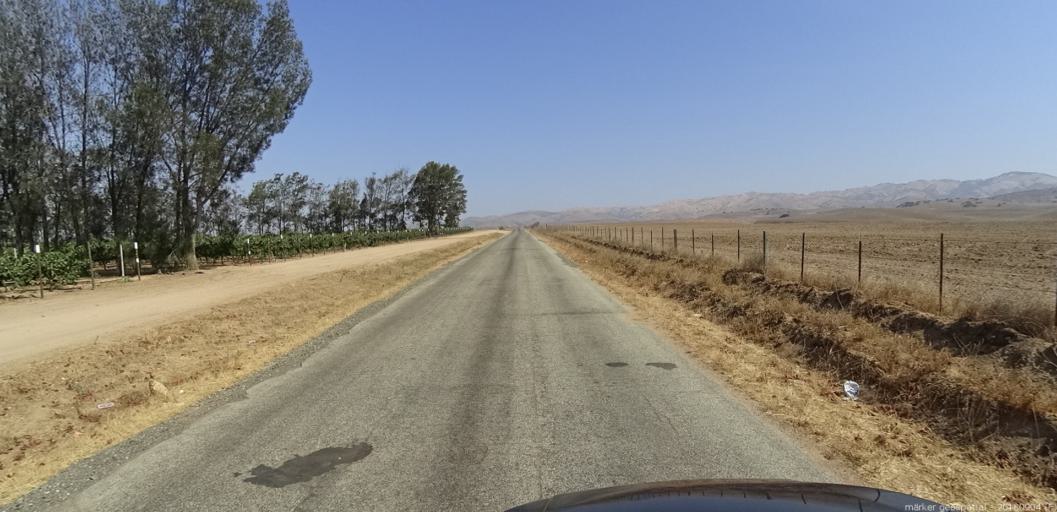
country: US
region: California
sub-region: Monterey County
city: Gonzales
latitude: 36.4967
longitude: -121.3648
